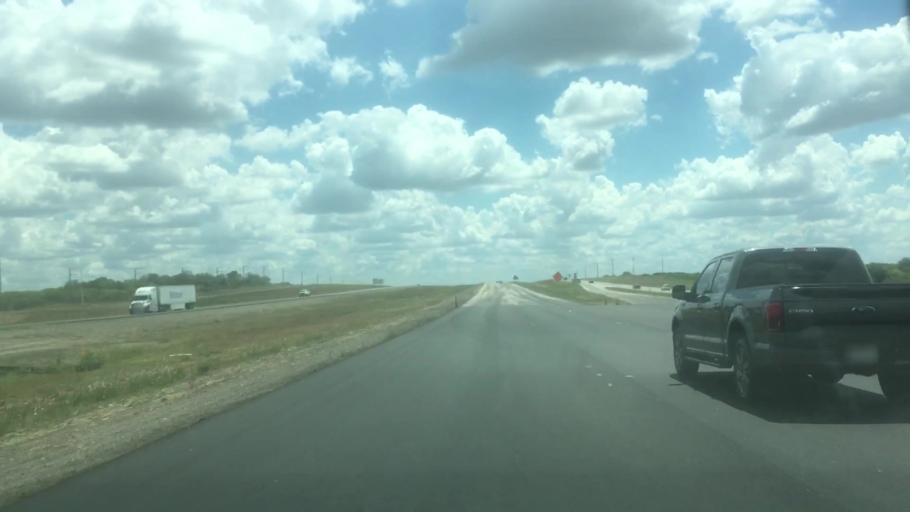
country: US
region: Texas
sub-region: Caldwell County
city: Lockhart
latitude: 29.9864
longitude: -97.6829
